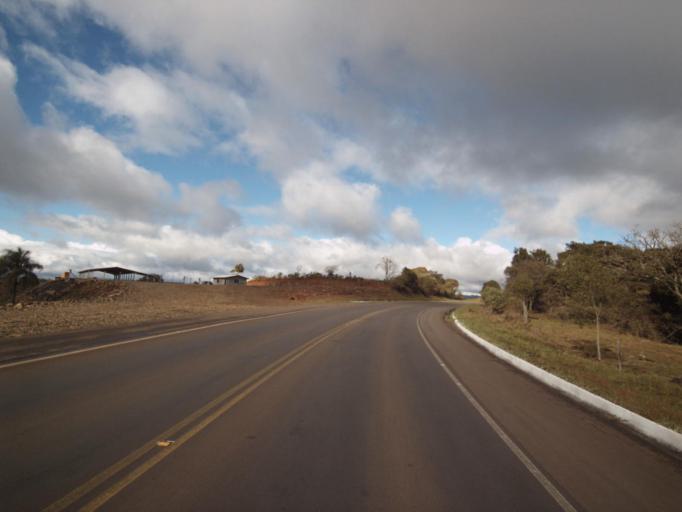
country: BR
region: Santa Catarina
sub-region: Concordia
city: Concordia
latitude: -27.1065
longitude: -51.9002
